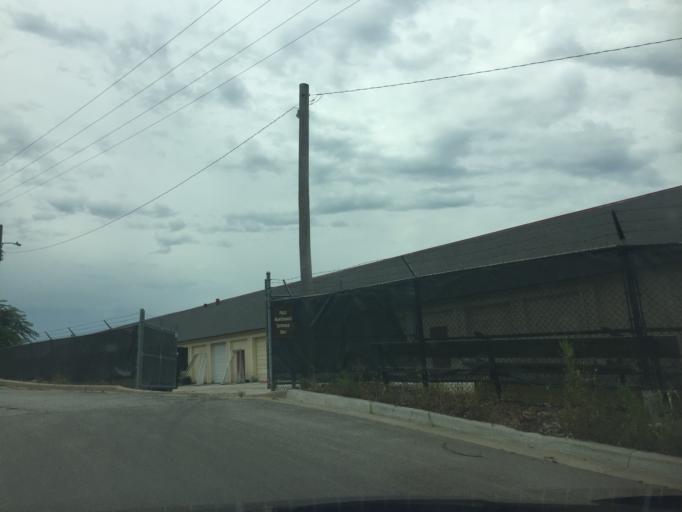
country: US
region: Kansas
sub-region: Leavenworth County
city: Leavenworth
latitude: 39.3620
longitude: -94.9197
